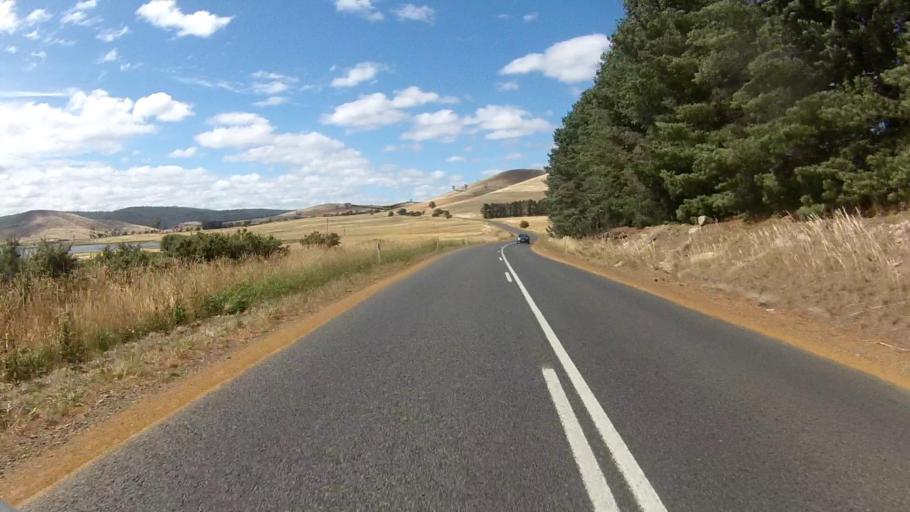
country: AU
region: Tasmania
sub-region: Brighton
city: Bridgewater
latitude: -42.5484
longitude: 147.3770
